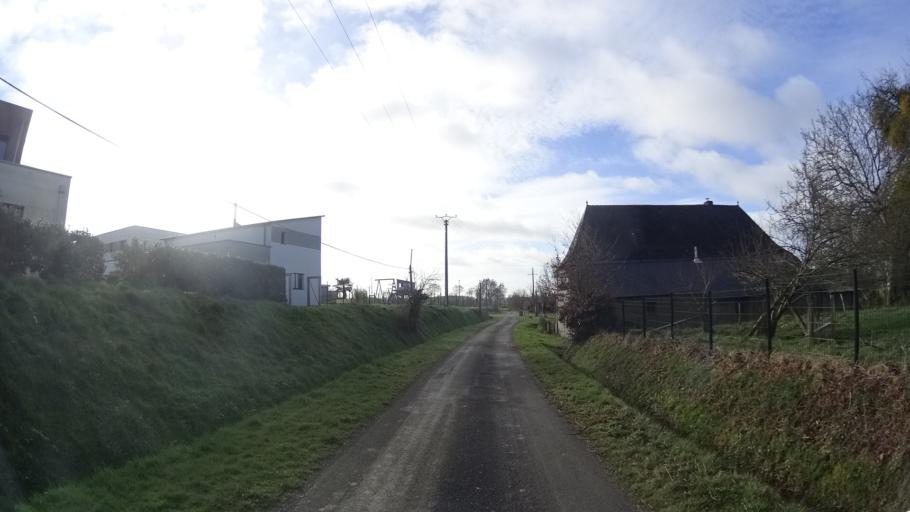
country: FR
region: Brittany
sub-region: Departement d'Ille-et-Vilaine
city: Romille
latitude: 48.2162
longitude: -1.9057
